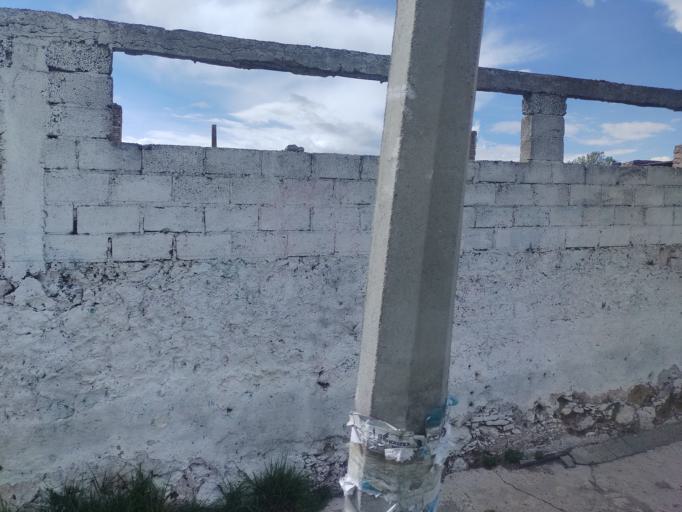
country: MX
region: Mexico
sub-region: Aculco
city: El Colorado
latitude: 20.1061
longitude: -99.7269
